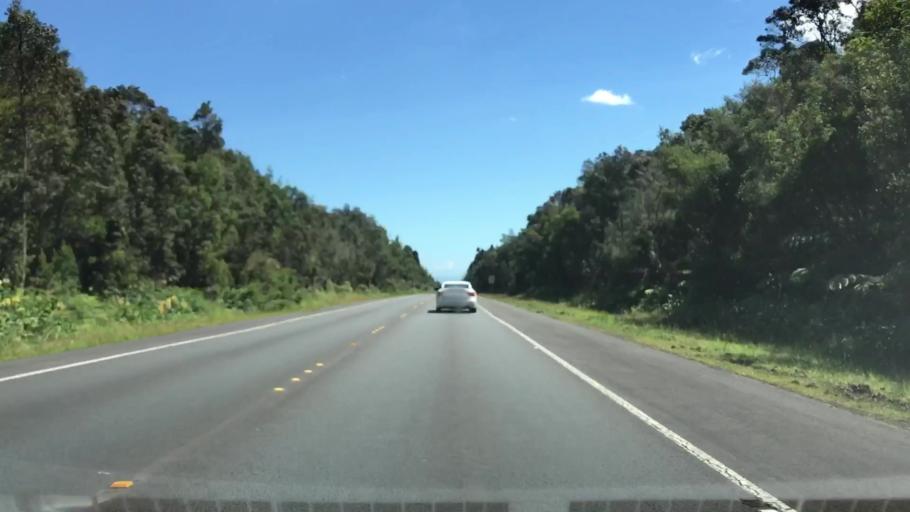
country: US
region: Hawaii
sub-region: Hawaii County
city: Volcano
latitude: 19.4277
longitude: -155.2319
